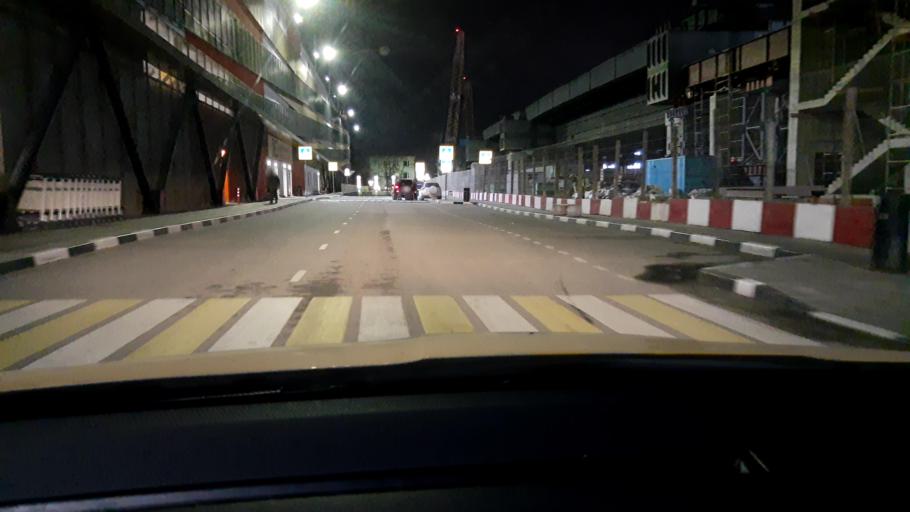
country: RU
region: Moskovskaya
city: Lobnya
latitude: 55.9825
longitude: 37.4127
